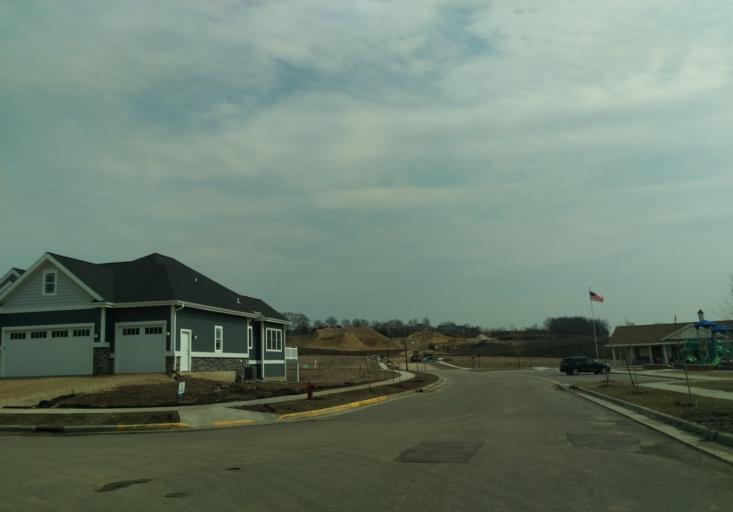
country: US
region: Wisconsin
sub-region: Dane County
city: Waunakee
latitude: 43.1743
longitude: -89.4528
